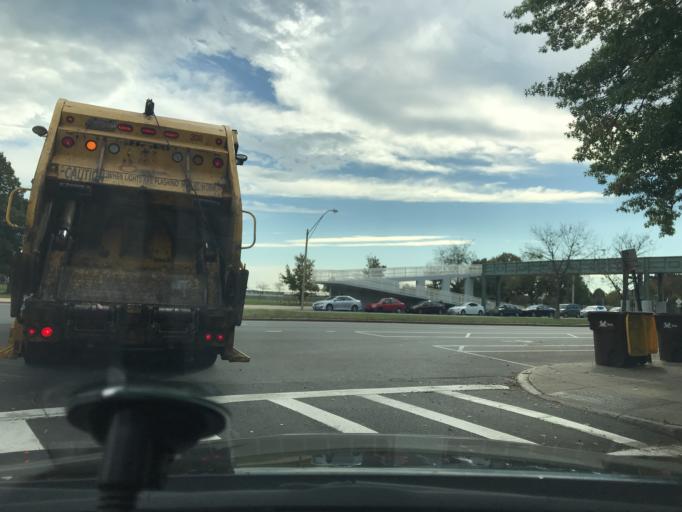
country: US
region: Massachusetts
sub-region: Suffolk County
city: South Boston
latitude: 42.3269
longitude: -71.0527
